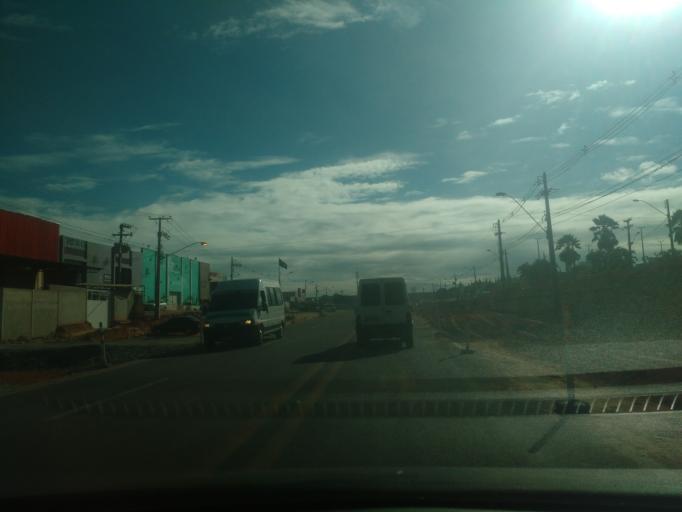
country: BR
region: Alagoas
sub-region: Satuba
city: Satuba
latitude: -9.5642
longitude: -35.7737
